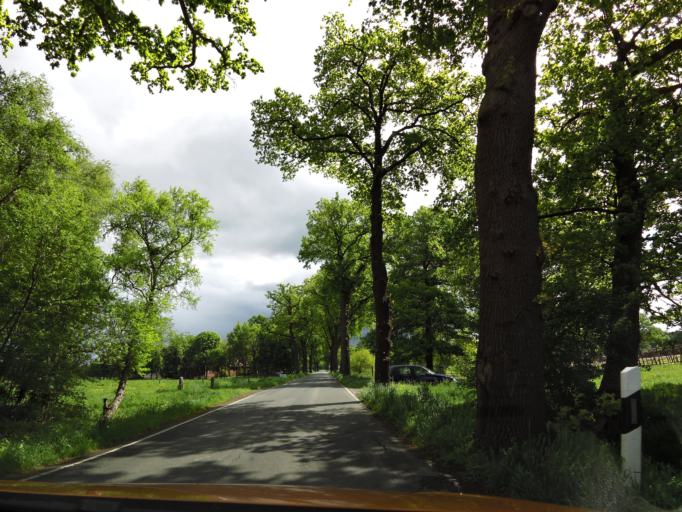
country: DE
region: Lower Saxony
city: Hude
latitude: 53.1525
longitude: 8.4356
